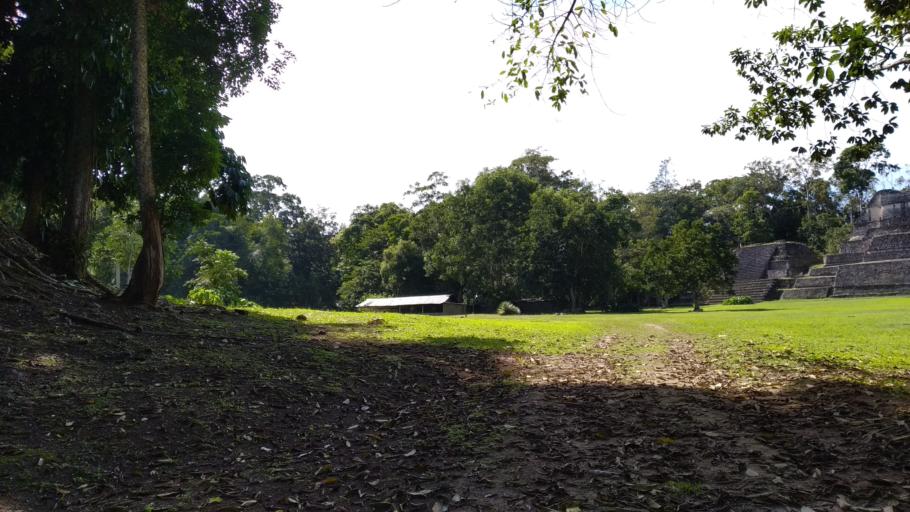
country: GT
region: Peten
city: Melchor de Mencos
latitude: 16.7623
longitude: -89.1196
